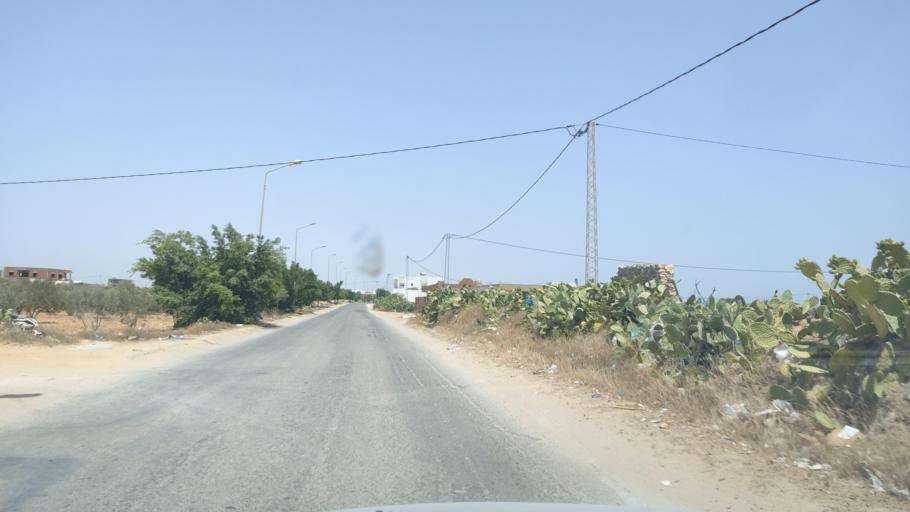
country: TN
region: Safaqis
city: Sfax
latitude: 34.6759
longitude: 10.7176
